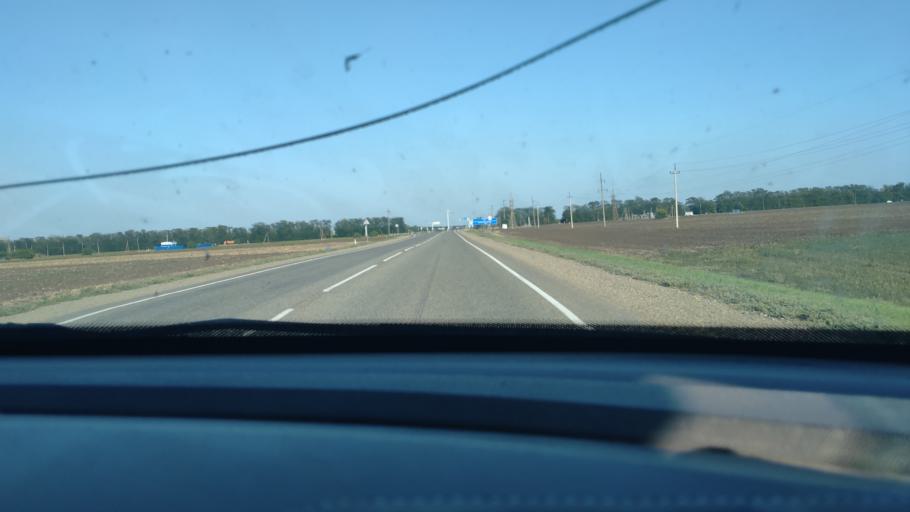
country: RU
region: Krasnodarskiy
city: Staroshcherbinovskaya
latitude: 46.6105
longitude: 38.6483
